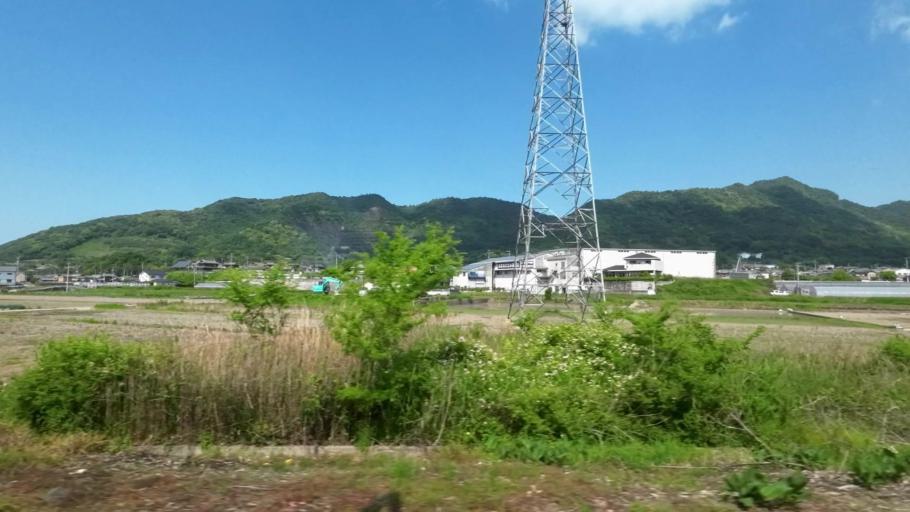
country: JP
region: Kagawa
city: Kan'onjicho
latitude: 34.1474
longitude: 133.6865
